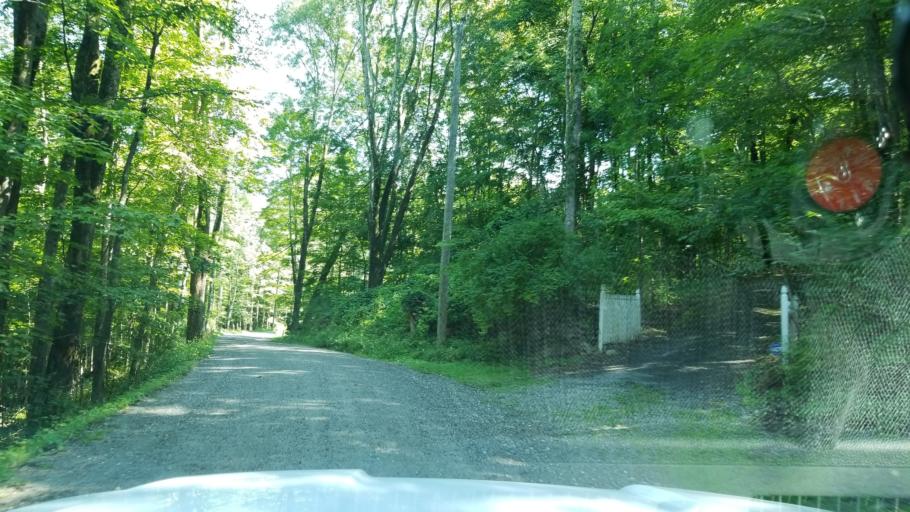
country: US
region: Connecticut
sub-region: Litchfield County
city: Kent
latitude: 41.7701
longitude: -73.4195
